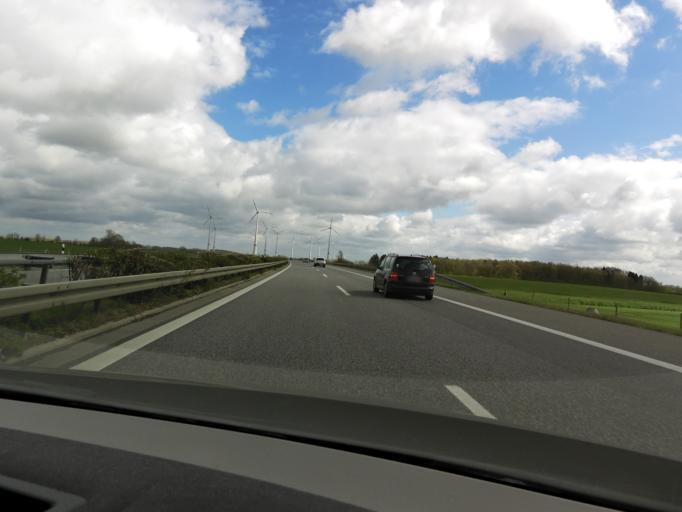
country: DE
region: Mecklenburg-Vorpommern
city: Grimmen
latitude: 54.0816
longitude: 13.0081
